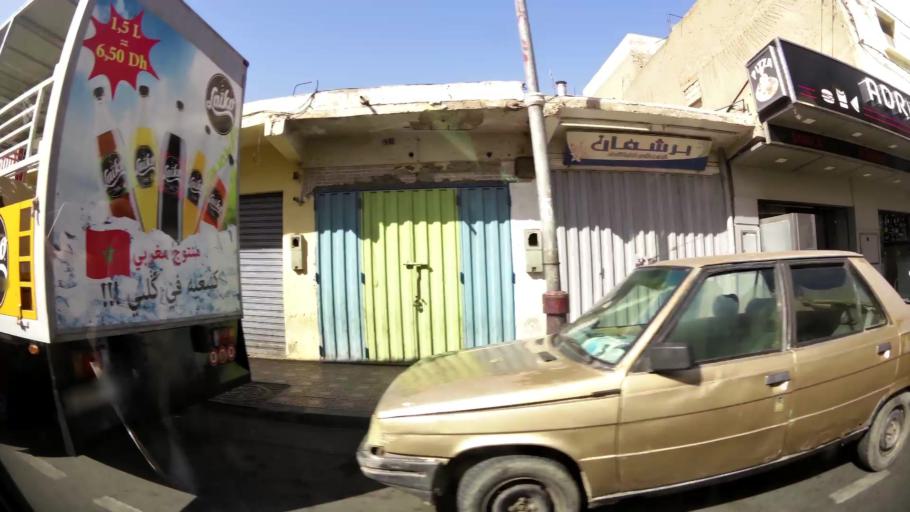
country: MA
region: Souss-Massa-Draa
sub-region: Inezgane-Ait Mellou
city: Inezgane
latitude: 30.3708
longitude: -9.5403
